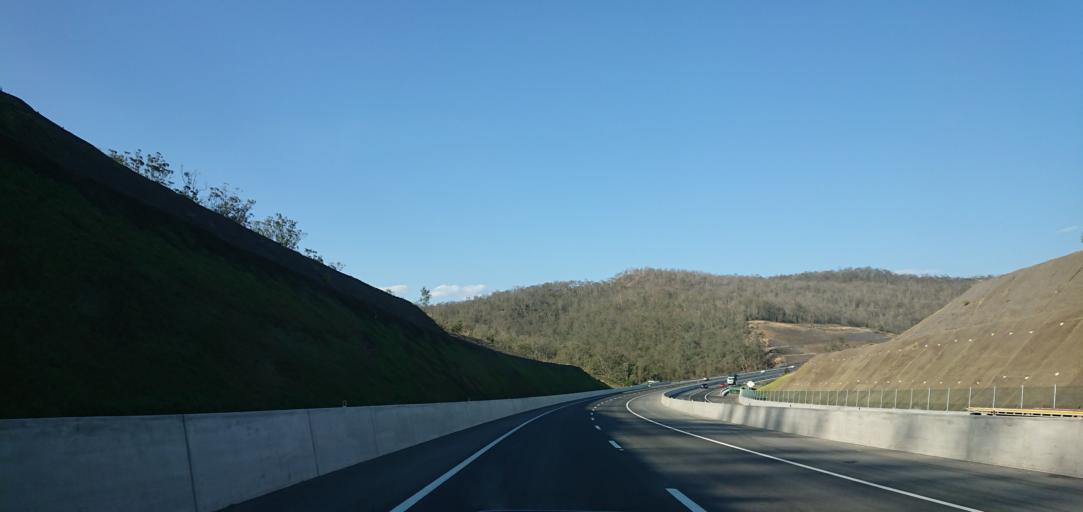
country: AU
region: Queensland
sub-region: Toowoomba
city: Wilsonton Heights
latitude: -27.4999
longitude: 151.9762
